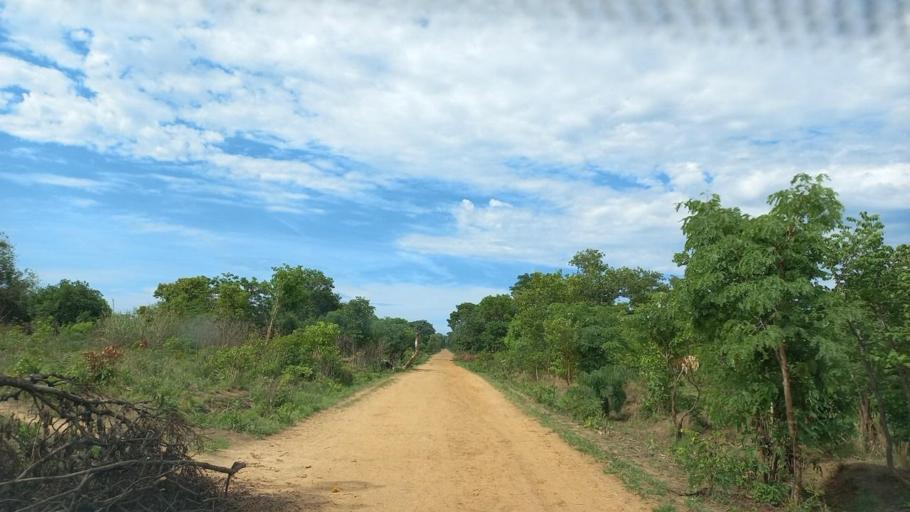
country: ZM
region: North-Western
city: Kabompo
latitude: -13.5248
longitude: 24.3812
